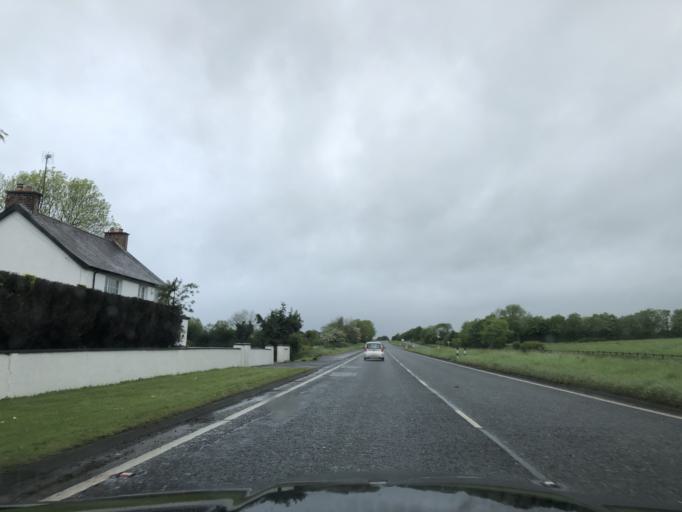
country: GB
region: Northern Ireland
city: Connor
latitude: 54.7979
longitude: -6.2564
